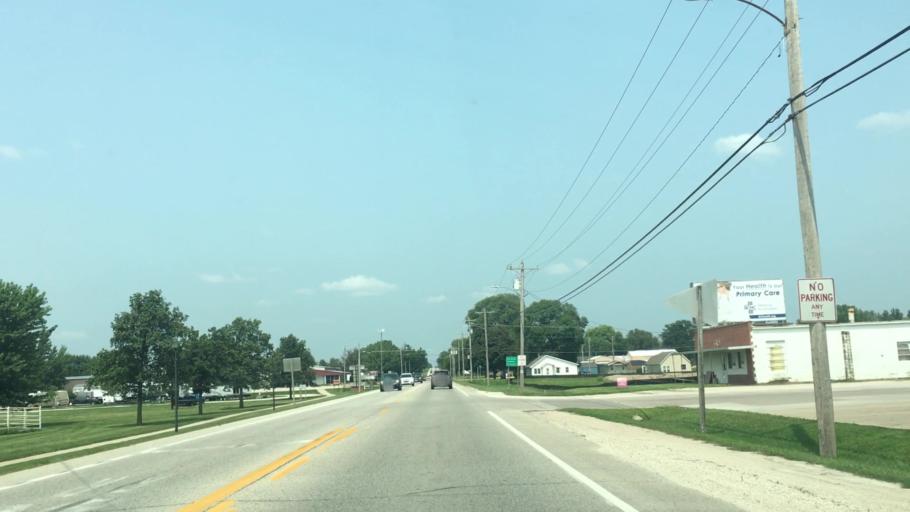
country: US
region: Iowa
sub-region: Buchanan County
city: Independence
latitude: 42.4800
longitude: -91.8894
